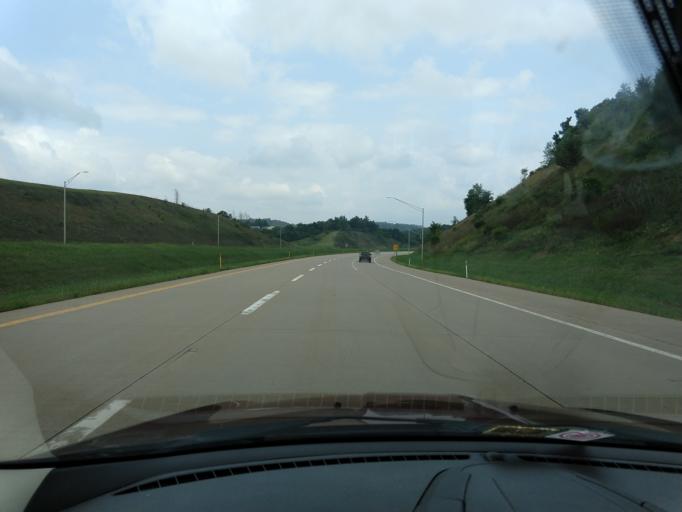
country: US
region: Pennsylvania
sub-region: Washington County
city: Gastonville
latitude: 40.2462
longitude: -79.9813
